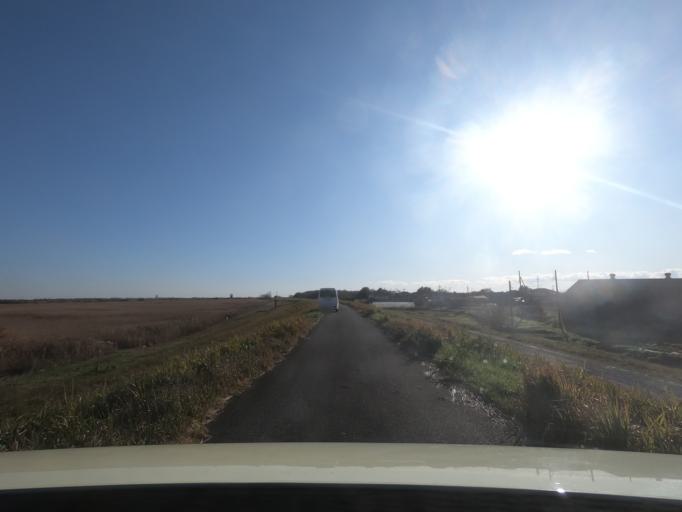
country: JP
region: Tochigi
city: Fujioka
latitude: 36.2723
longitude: 139.6802
